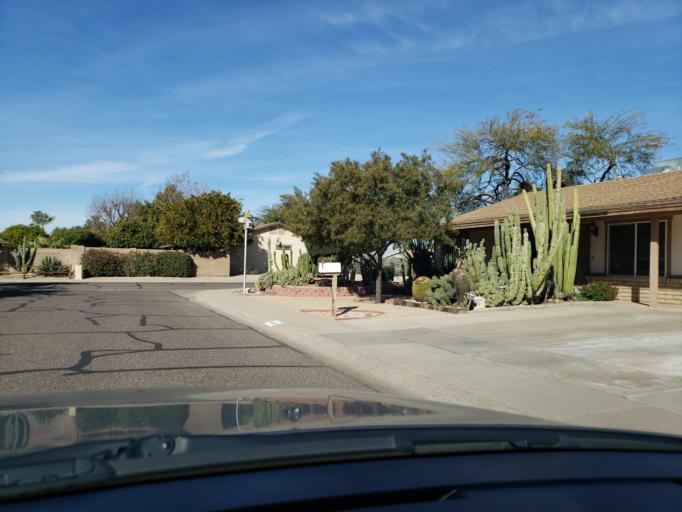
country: US
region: Arizona
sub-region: Maricopa County
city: Paradise Valley
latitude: 33.6015
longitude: -111.9932
